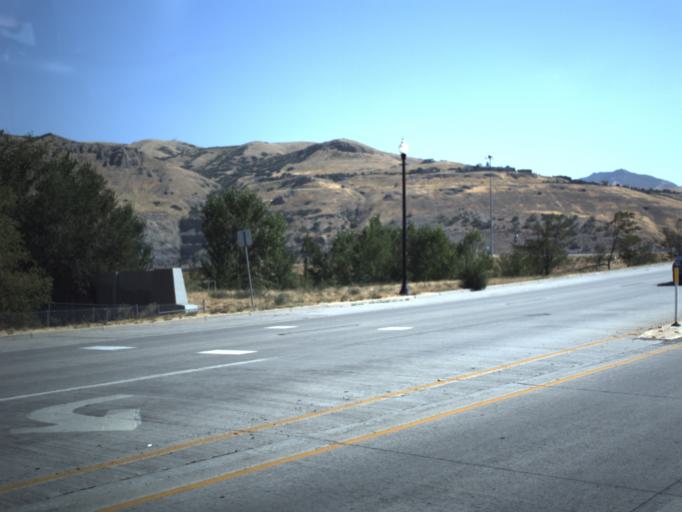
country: US
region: Utah
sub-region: Salt Lake County
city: Salt Lake City
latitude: 40.7823
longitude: -111.9135
